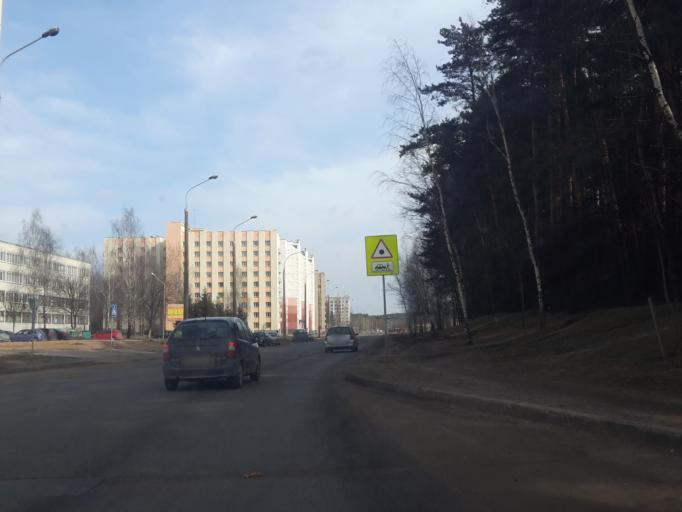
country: BY
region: Minsk
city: Vyaliki Trastsyanets
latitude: 53.8978
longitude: 27.6520
